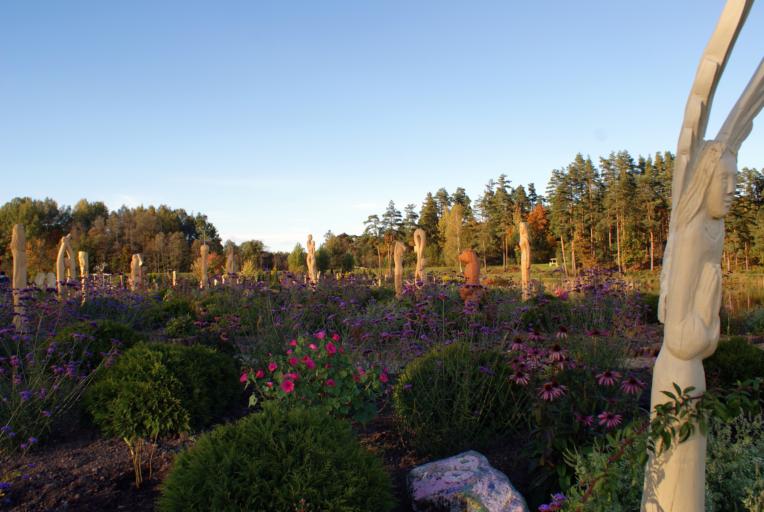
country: LV
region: Aglona
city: Aglona
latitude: 56.1260
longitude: 27.0375
